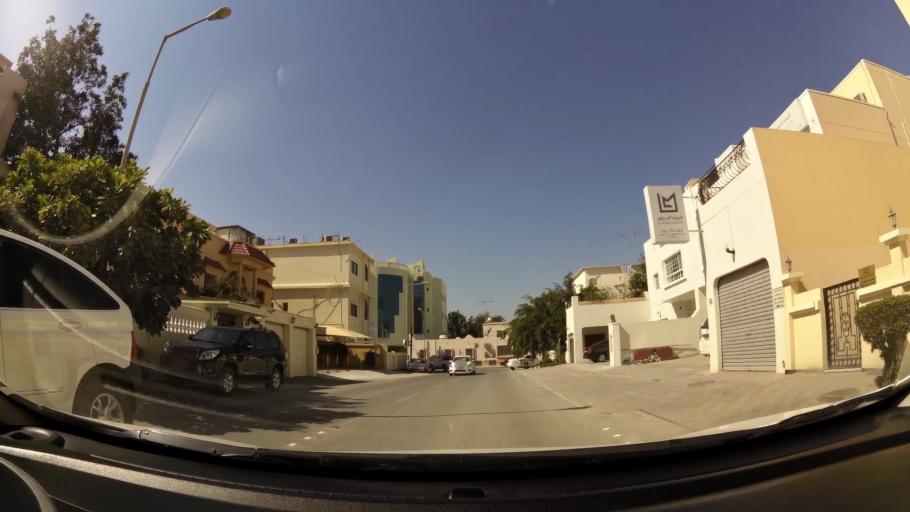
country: BH
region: Manama
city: Manama
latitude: 26.2061
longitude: 50.5791
